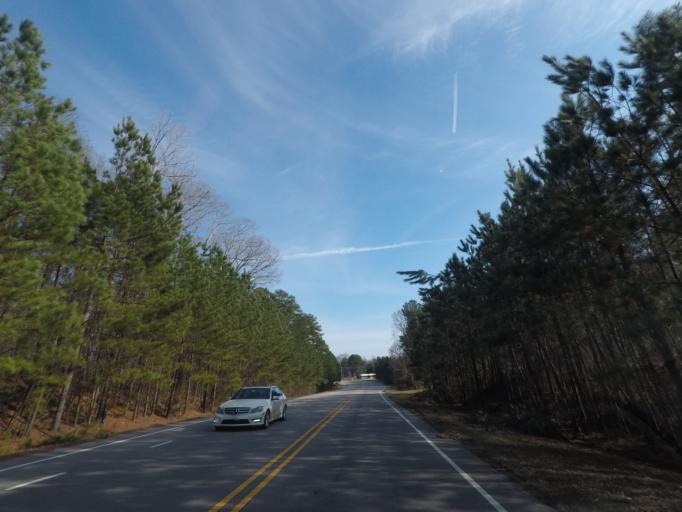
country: US
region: North Carolina
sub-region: Durham County
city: Durham
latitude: 36.0835
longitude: -78.9345
